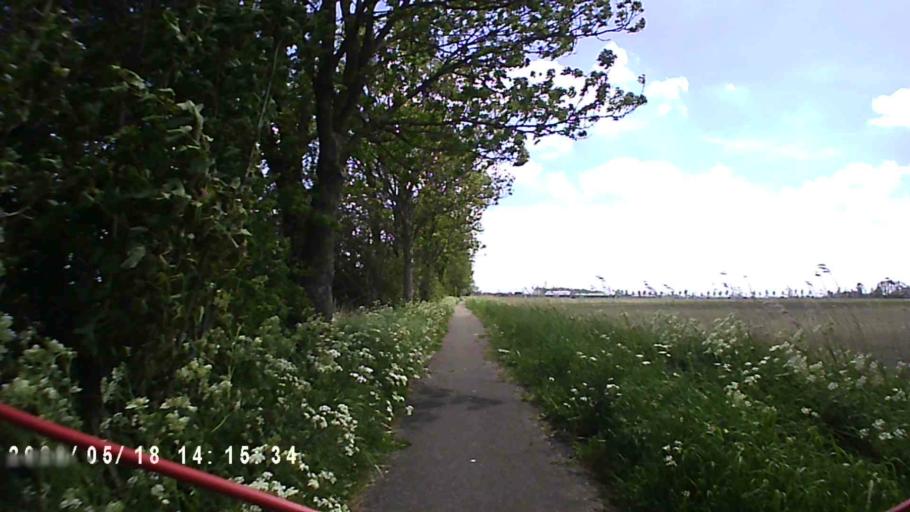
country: NL
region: Groningen
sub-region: Gemeente Winsum
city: Winsum
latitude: 53.3127
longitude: 6.4713
